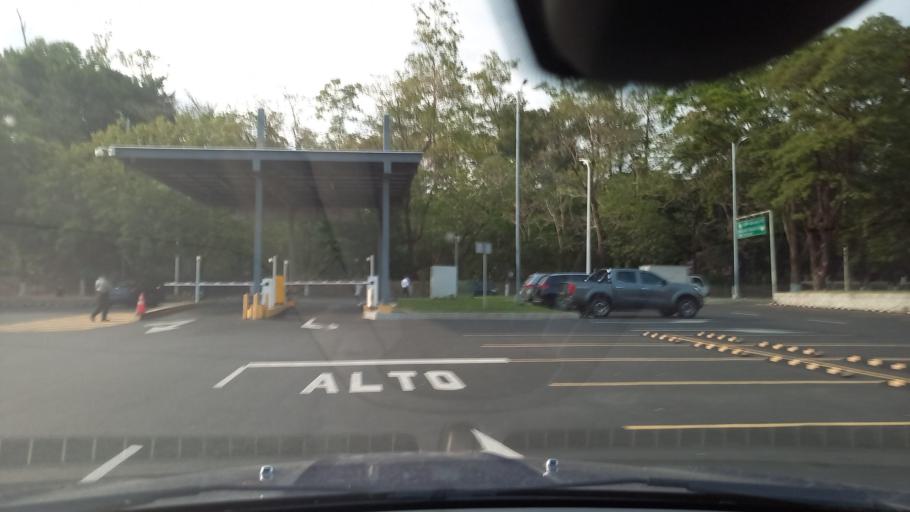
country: SV
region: La Paz
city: El Rosario
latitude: 13.4473
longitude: -89.0559
